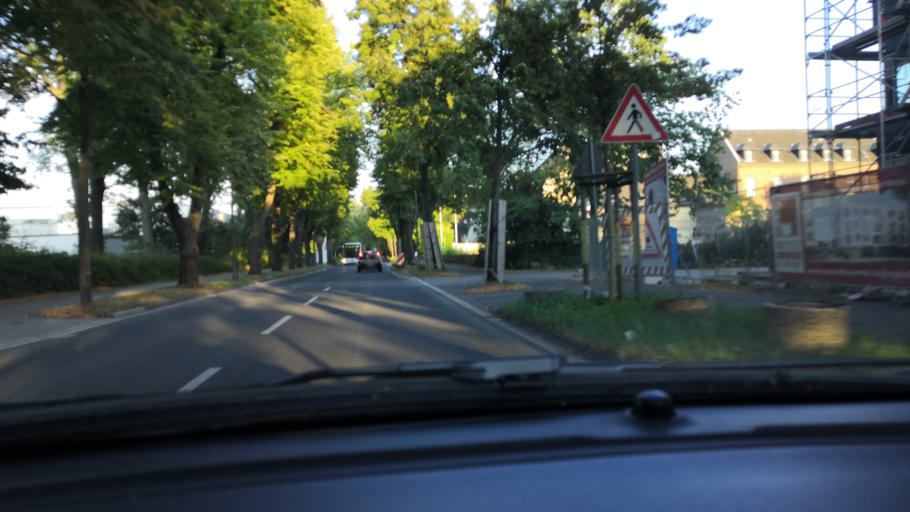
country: DE
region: North Rhine-Westphalia
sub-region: Regierungsbezirk Dusseldorf
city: Neuss
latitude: 51.1904
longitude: 6.7022
